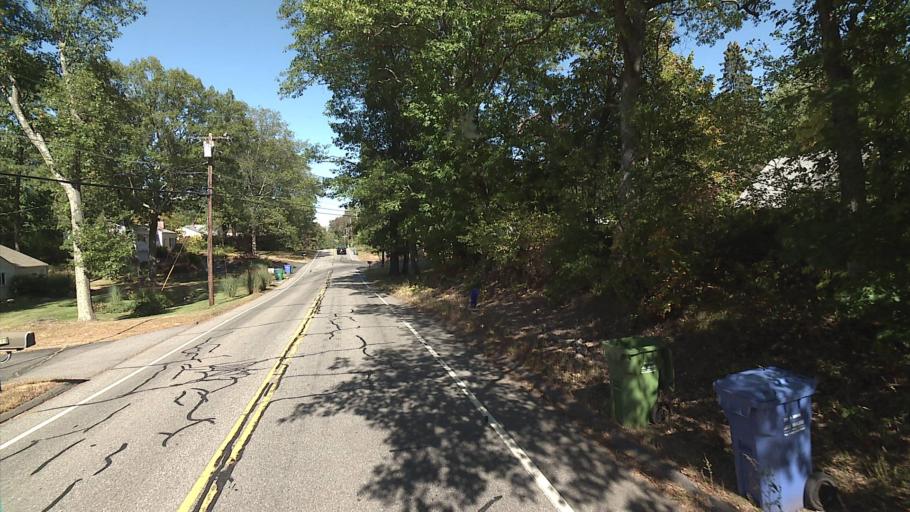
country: US
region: Connecticut
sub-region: Hartford County
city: Manchester
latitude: 41.7205
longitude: -72.5262
